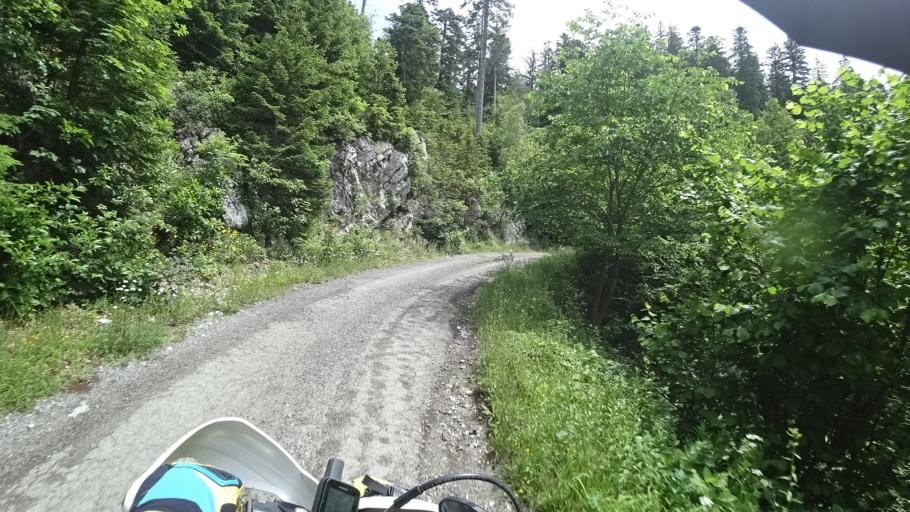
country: HR
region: Primorsko-Goranska
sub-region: Grad Delnice
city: Delnice
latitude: 45.3299
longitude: 14.7614
